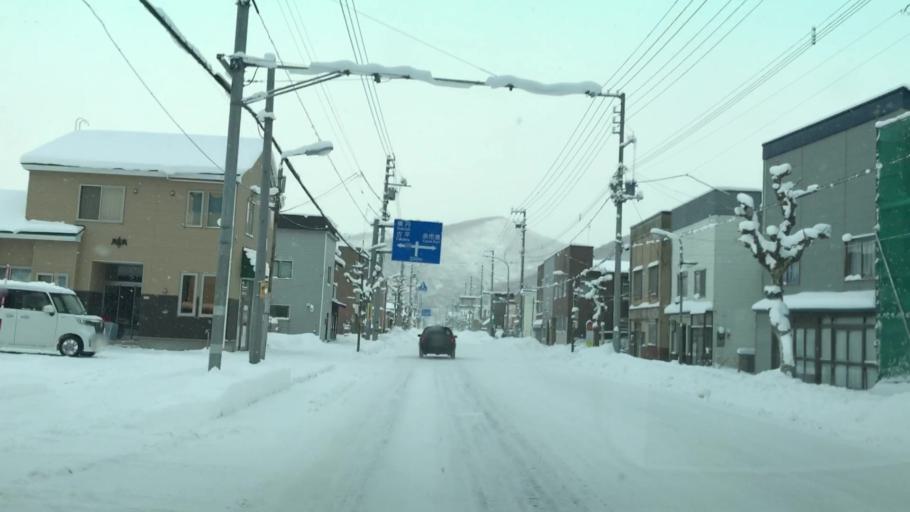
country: JP
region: Hokkaido
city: Yoichi
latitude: 43.2049
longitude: 140.7714
